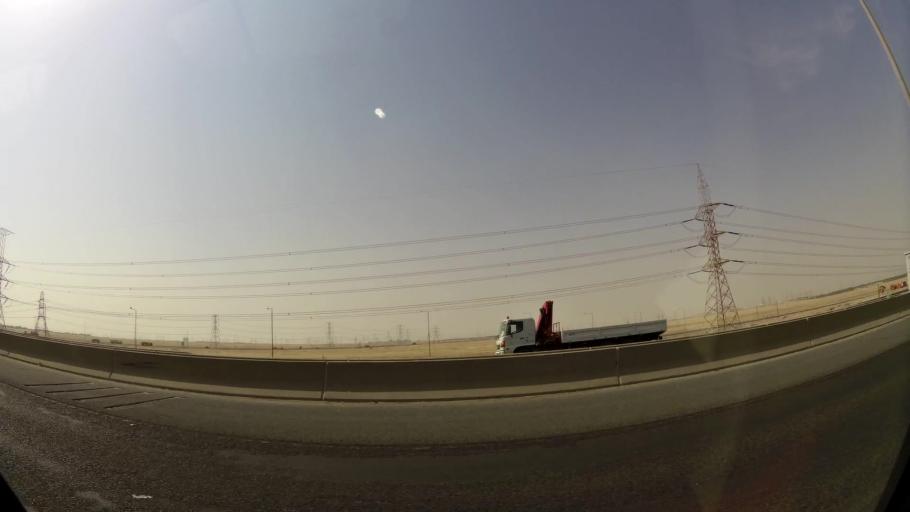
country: KW
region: Al Ahmadi
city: Al Fahahil
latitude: 29.0412
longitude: 48.1162
